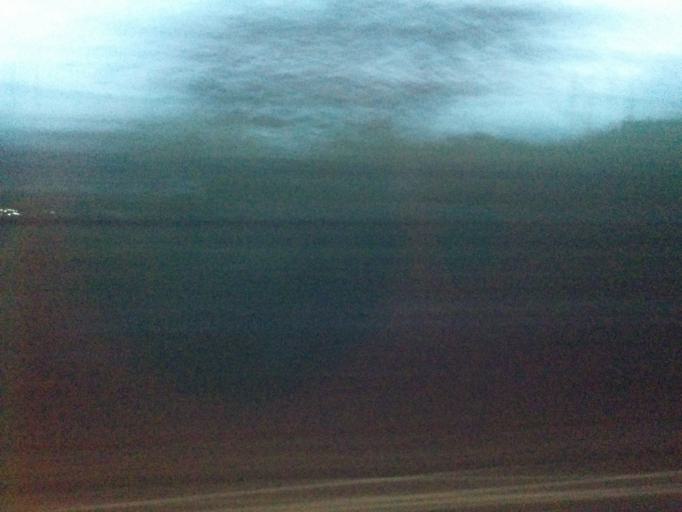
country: JP
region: Aichi
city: Obu
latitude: 35.0465
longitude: 136.9554
